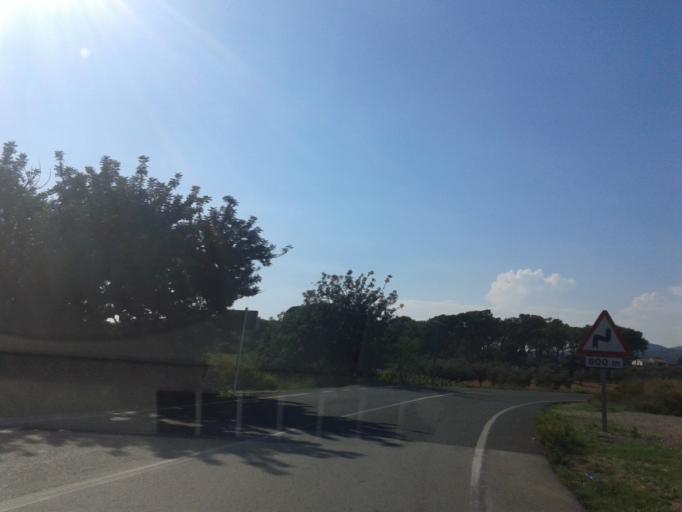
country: ES
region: Catalonia
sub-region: Provincia de Tarragona
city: Sant Jaume dels Domenys
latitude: 41.2818
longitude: 1.5446
